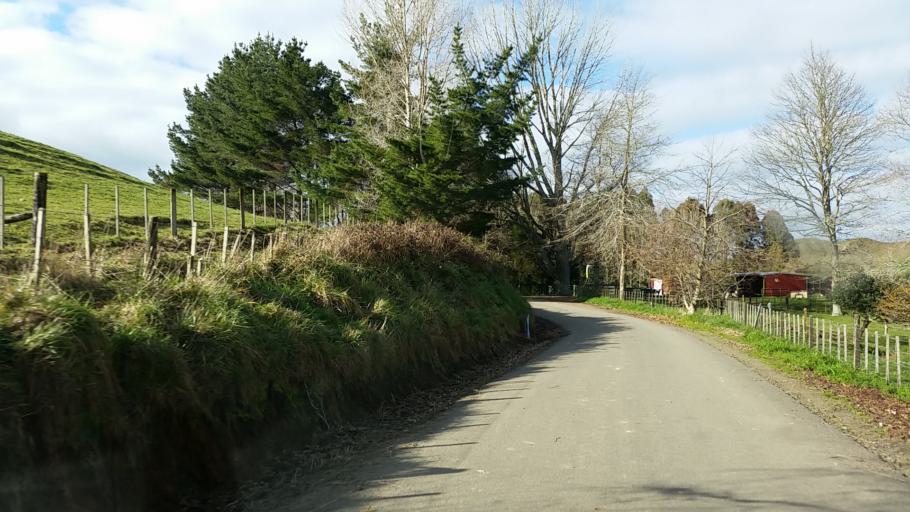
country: NZ
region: Taranaki
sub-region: South Taranaki District
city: Eltham
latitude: -39.2522
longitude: 174.5086
